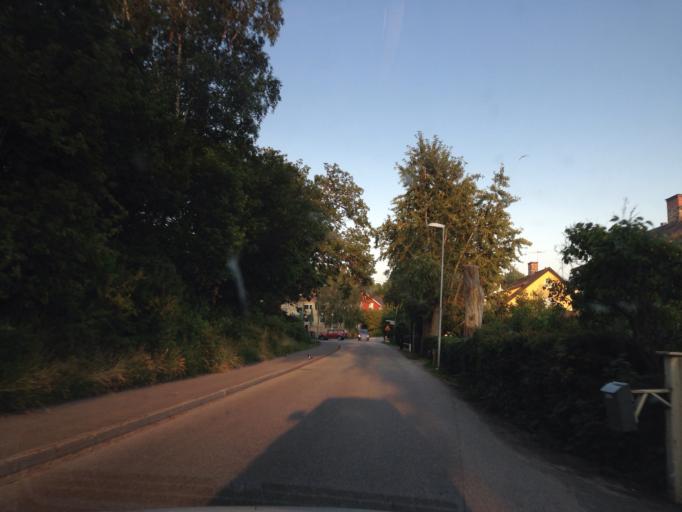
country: SE
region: Stockholm
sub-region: Varmdo Kommun
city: Gustavsberg
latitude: 59.3217
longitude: 18.3885
